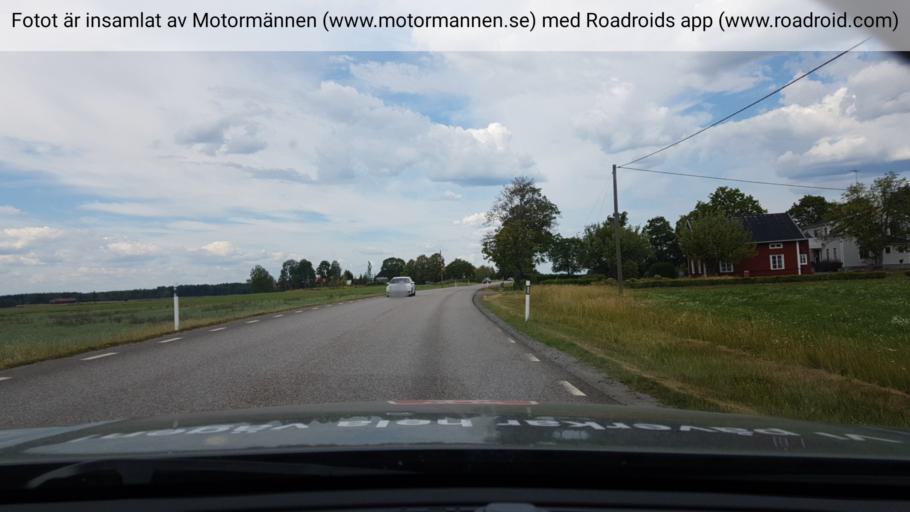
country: SE
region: Vaestmanland
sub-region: Sala Kommun
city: Sala
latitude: 59.8622
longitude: 16.6318
